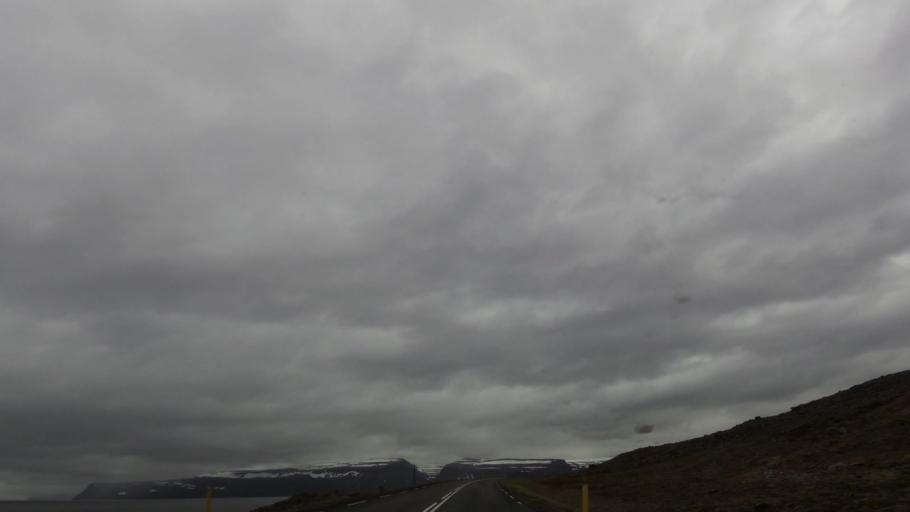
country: IS
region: Westfjords
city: Isafjoerdur
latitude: 66.0460
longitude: -22.7707
